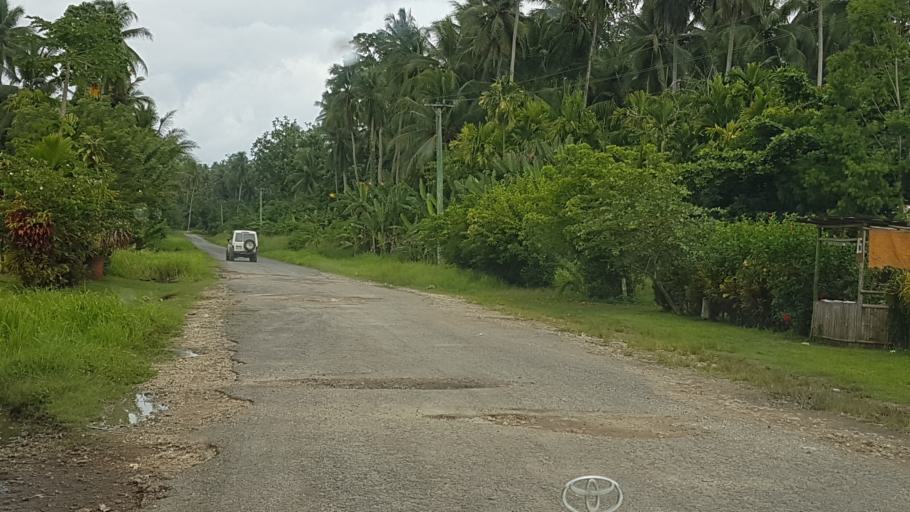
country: PG
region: Madang
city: Madang
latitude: -4.8056
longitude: 145.7461
